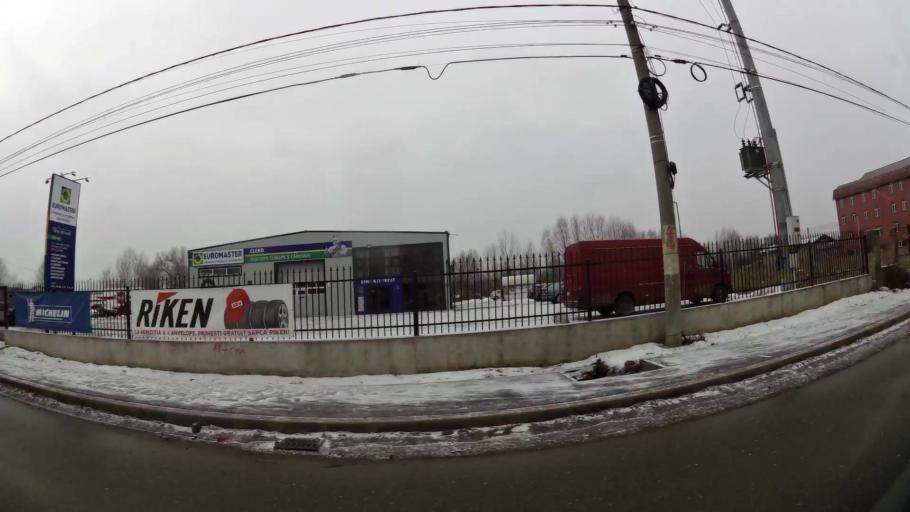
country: RO
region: Dambovita
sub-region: Municipiul Targoviste
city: Targoviste
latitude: 44.9344
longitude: 25.4741
